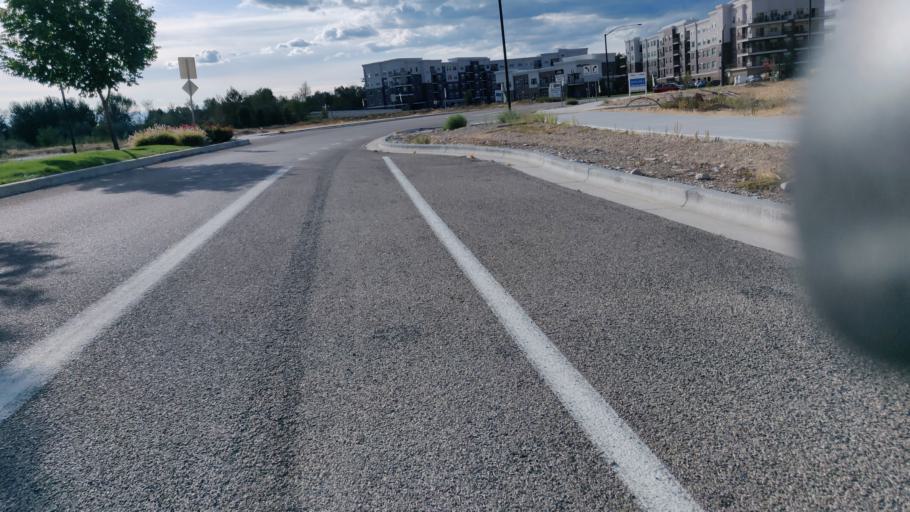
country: US
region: Idaho
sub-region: Ada County
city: Boise
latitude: 43.5766
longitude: -116.1475
